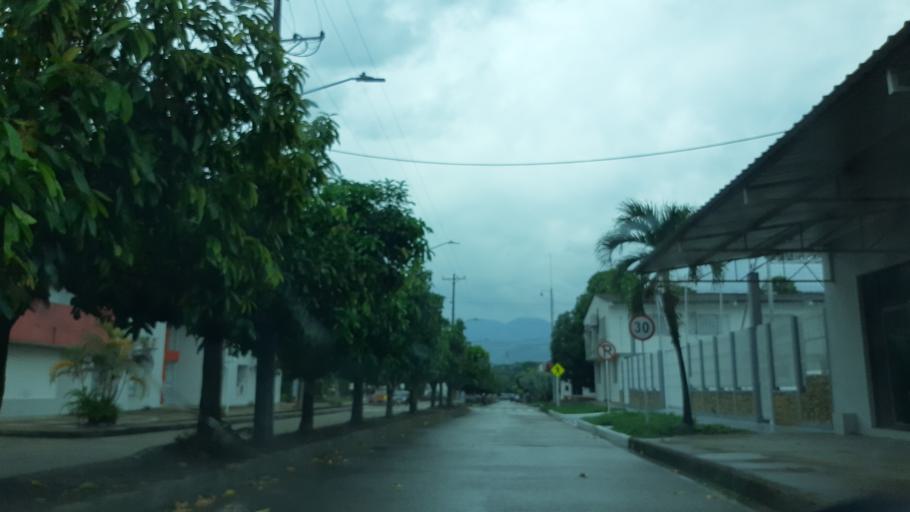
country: CO
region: Casanare
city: Monterrey
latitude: 4.8757
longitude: -72.8922
